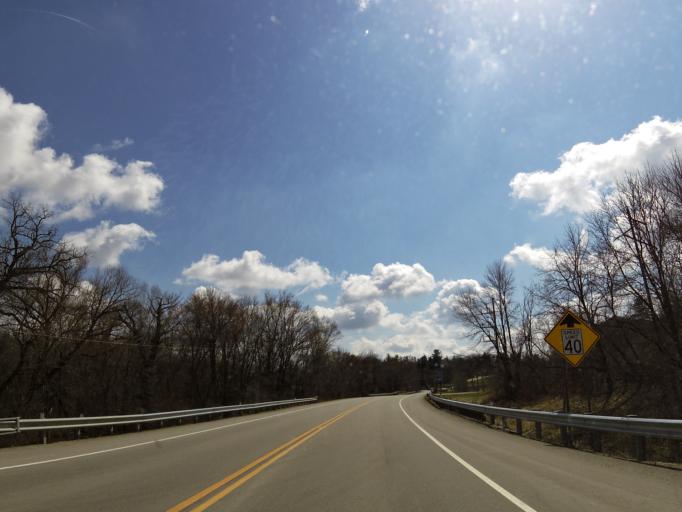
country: US
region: Minnesota
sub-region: Goodhue County
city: Kenyon
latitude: 44.2815
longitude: -92.9795
